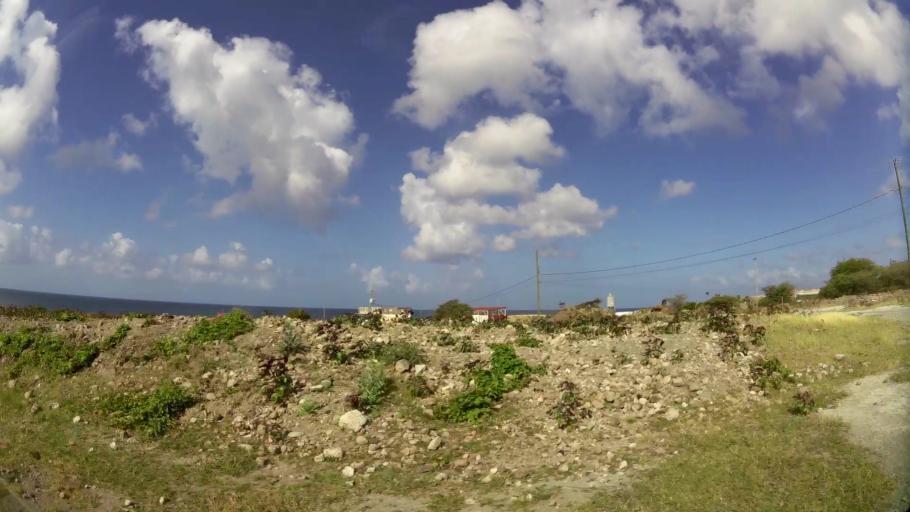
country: KN
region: Saint Paul Charlestown
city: Charlestown
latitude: 17.1148
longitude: -62.6202
